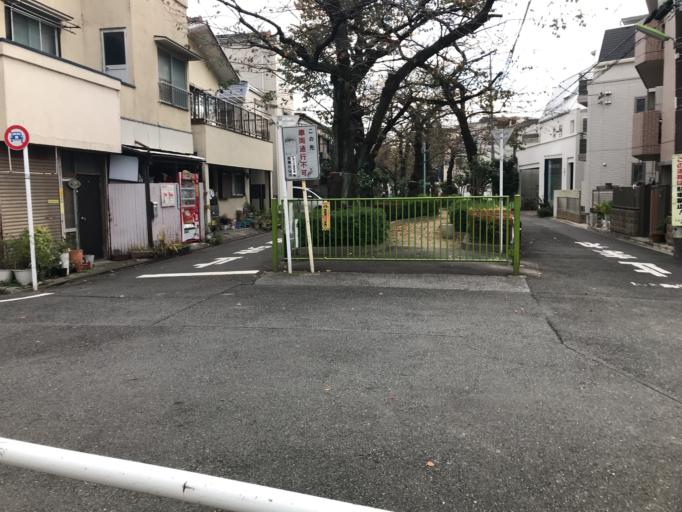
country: JP
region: Tokyo
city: Tokyo
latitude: 35.6080
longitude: 139.6771
